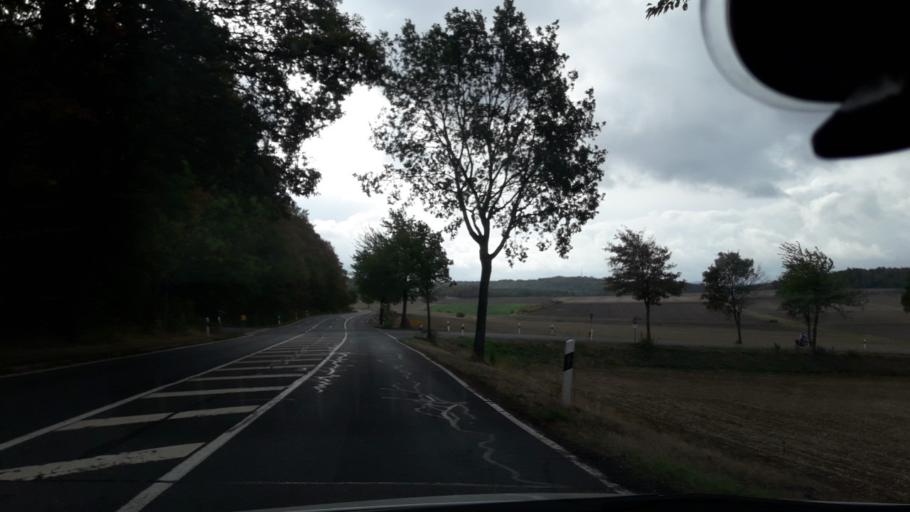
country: DE
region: Lower Saxony
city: Liebenburg
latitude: 51.9824
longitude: 10.4430
